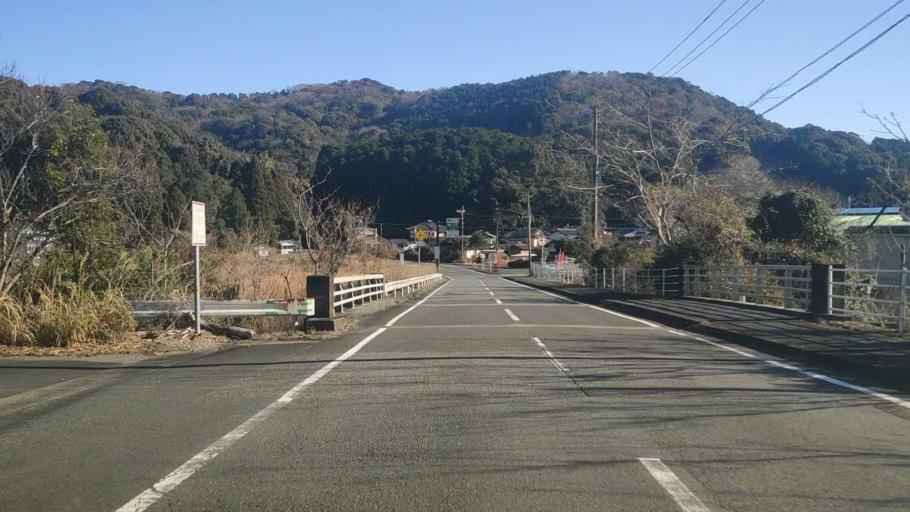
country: JP
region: Miyazaki
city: Nobeoka
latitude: 32.6880
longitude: 131.8067
